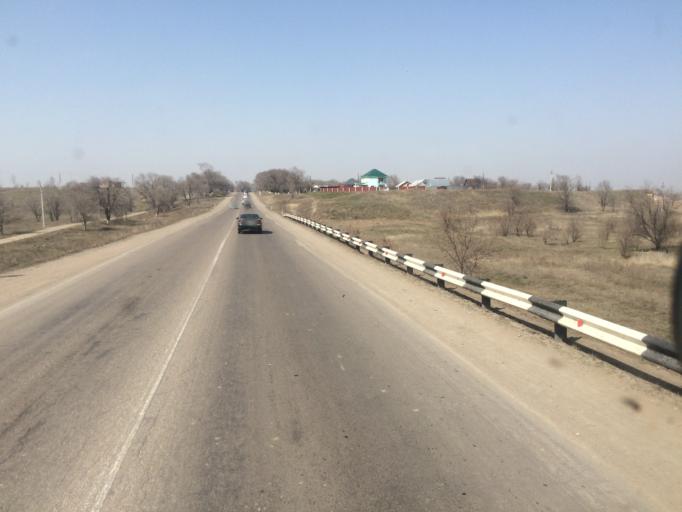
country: KZ
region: Almaty Oblysy
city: Burunday
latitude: 43.3045
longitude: 76.6710
